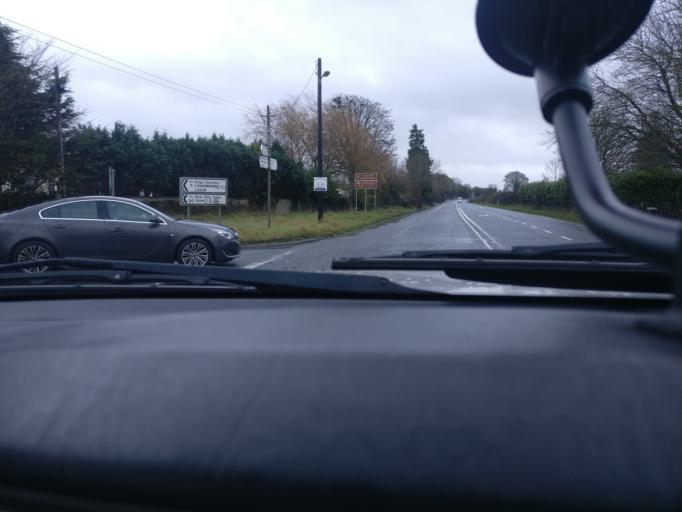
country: IE
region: Leinster
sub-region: An Mhi
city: Longwood
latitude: 53.4258
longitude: -6.8904
